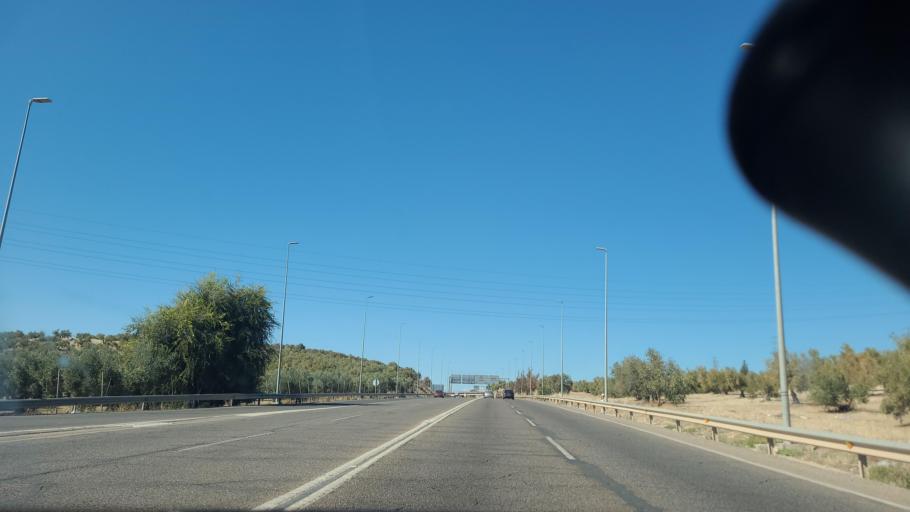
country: ES
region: Andalusia
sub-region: Provincia de Jaen
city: Jaen
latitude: 37.7836
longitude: -3.7682
